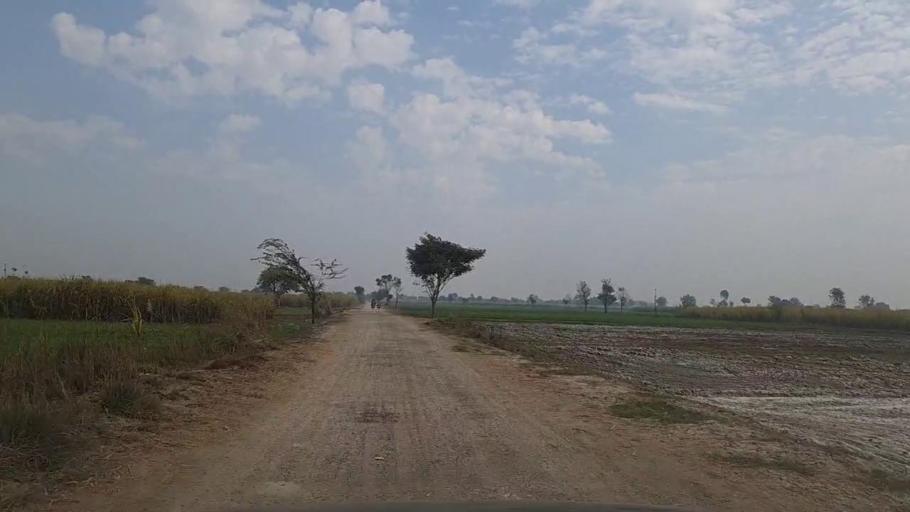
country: PK
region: Sindh
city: Daur
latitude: 26.3916
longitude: 68.3522
